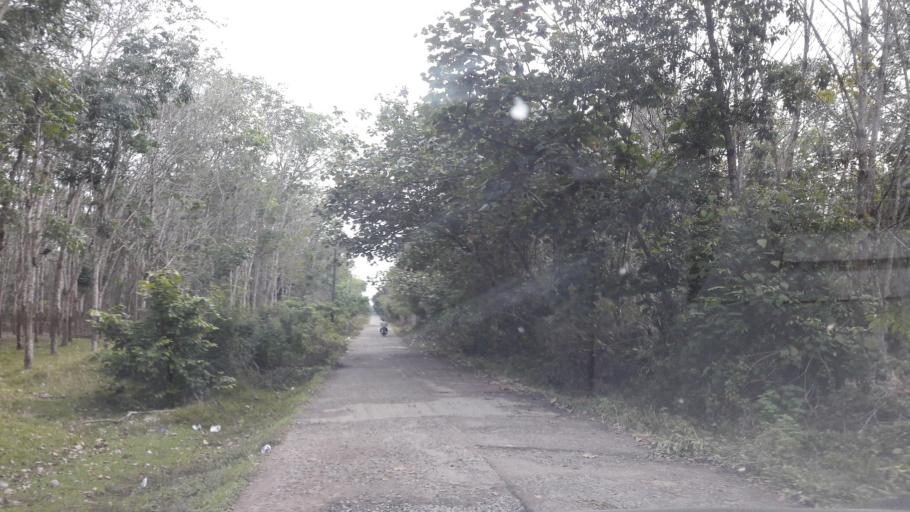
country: ID
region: South Sumatra
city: Gunungmenang
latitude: -3.1034
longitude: 104.0646
